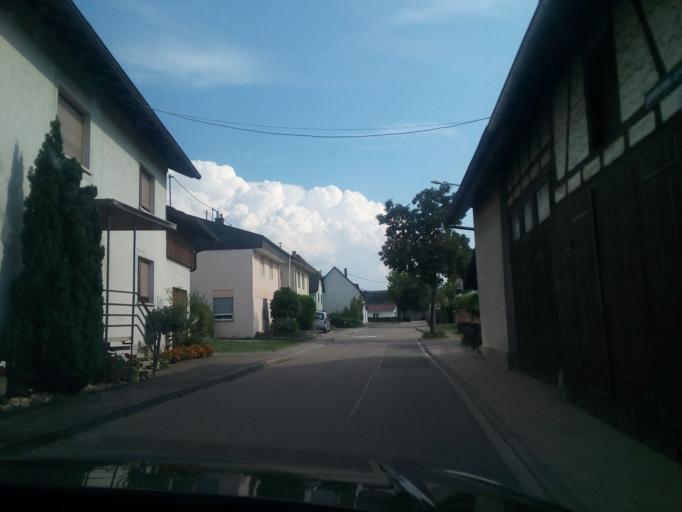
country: DE
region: Baden-Wuerttemberg
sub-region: Karlsruhe Region
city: Ottenhofen
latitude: 48.7371
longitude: 8.1306
